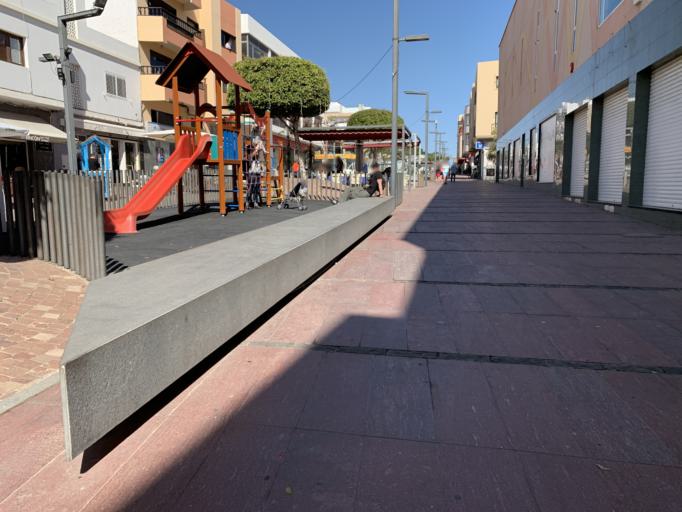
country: ES
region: Canary Islands
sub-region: Provincia de Las Palmas
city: Puerto del Rosario
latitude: 28.4968
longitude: -13.8611
